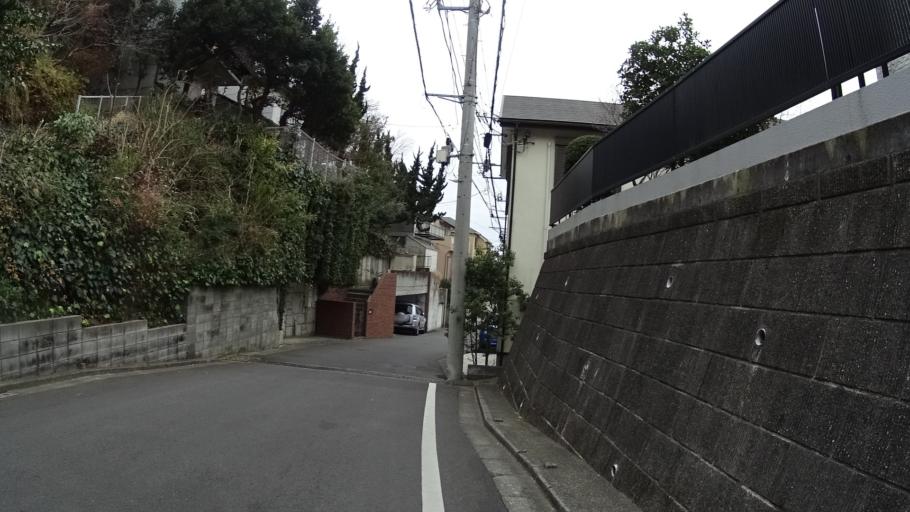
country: JP
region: Kanagawa
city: Oiso
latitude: 35.3142
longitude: 139.3074
